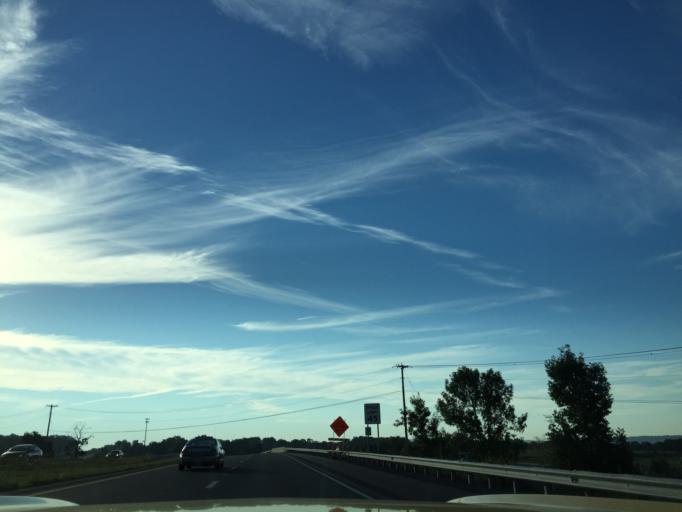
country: US
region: Pennsylvania
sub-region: Lehigh County
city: Ancient Oaks
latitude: 40.5645
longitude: -75.5883
